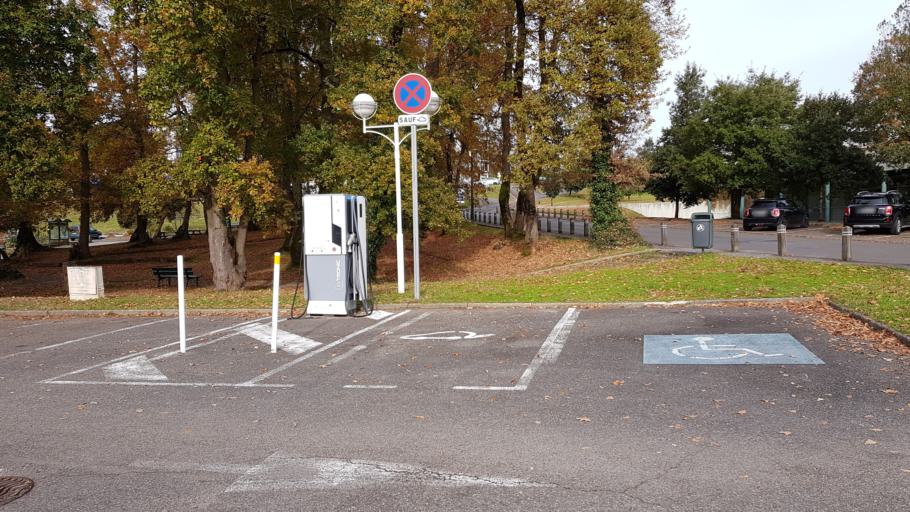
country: FR
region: Aquitaine
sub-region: Departement des Landes
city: Saint-Paul-les-Dax
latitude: 43.7278
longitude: -1.0644
